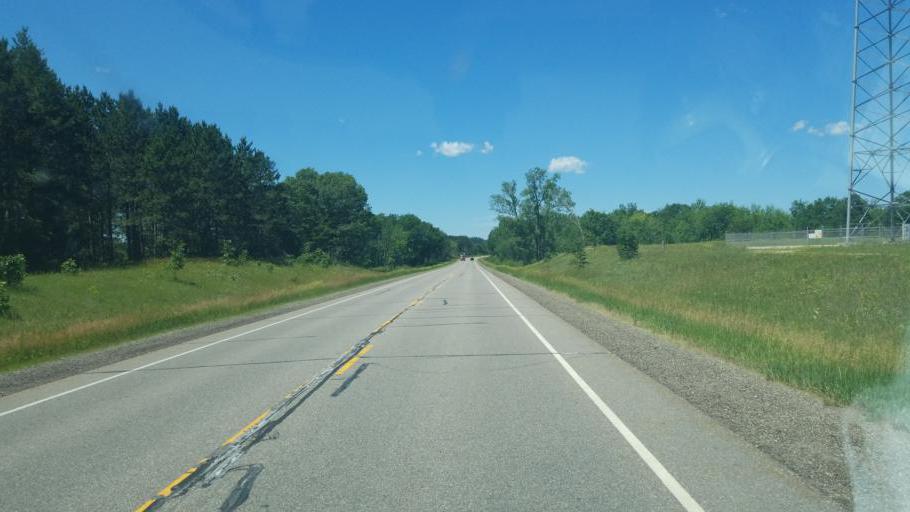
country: US
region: Wisconsin
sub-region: Adams County
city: Friendship
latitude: 44.0468
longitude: -89.9830
